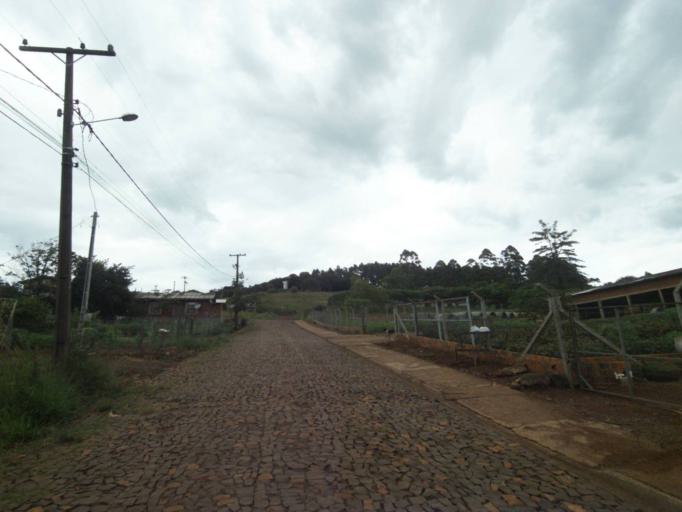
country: BR
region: Parana
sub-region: Guaraniacu
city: Guaraniacu
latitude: -25.1162
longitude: -52.8527
